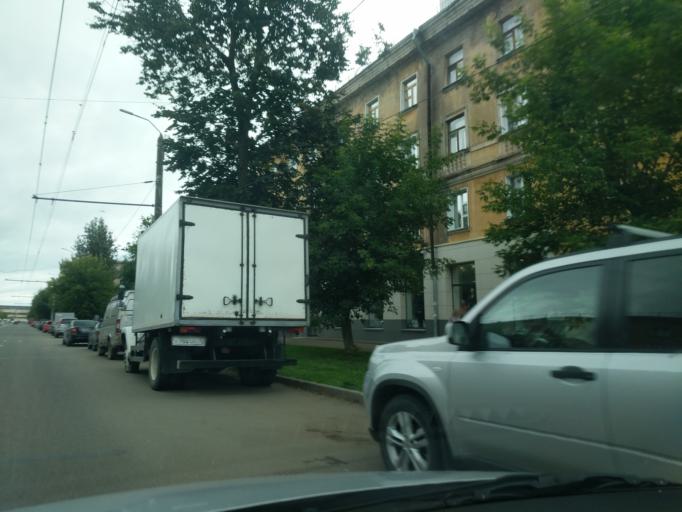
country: RU
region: Kirov
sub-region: Kirovo-Chepetskiy Rayon
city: Kirov
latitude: 58.6379
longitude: 49.6146
